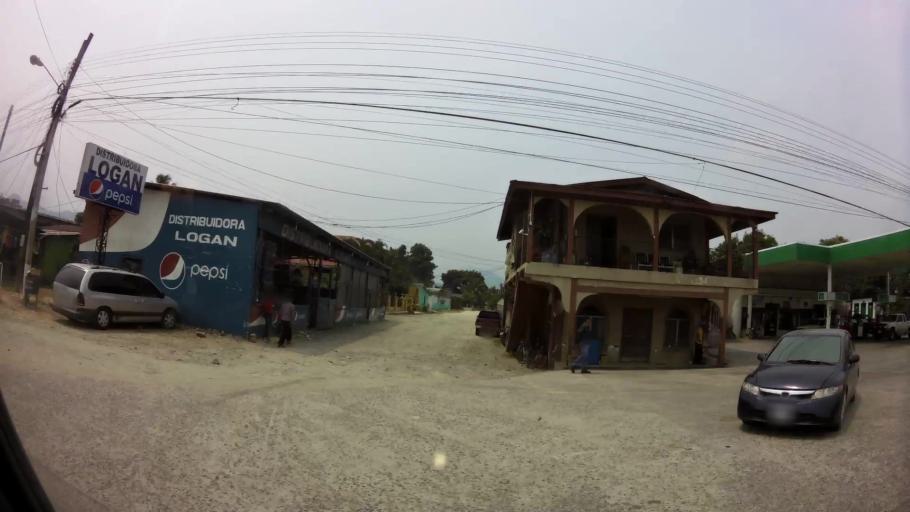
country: HN
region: Atlantida
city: San Juan Pueblo
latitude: 15.5988
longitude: -87.2123
